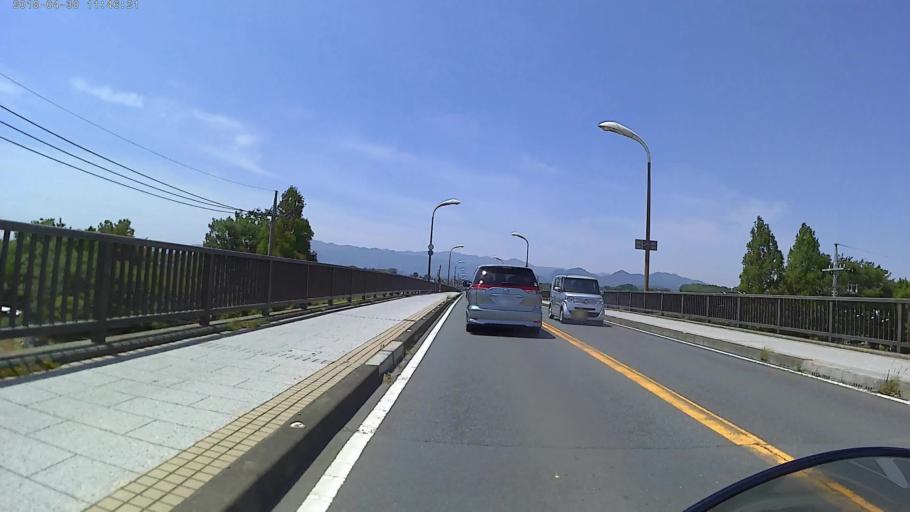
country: JP
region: Kanagawa
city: Zama
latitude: 35.4867
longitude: 139.3773
